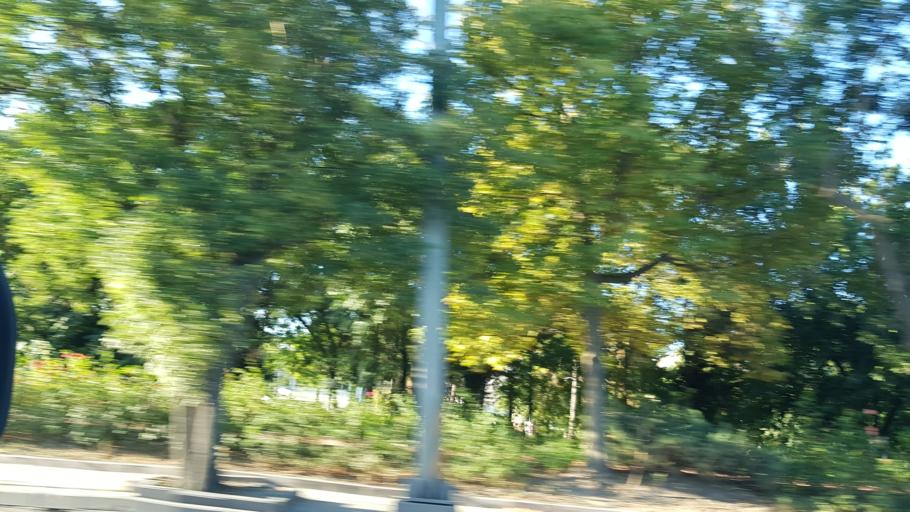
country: TR
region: Ankara
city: Ankara
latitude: 39.9536
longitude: 32.8120
